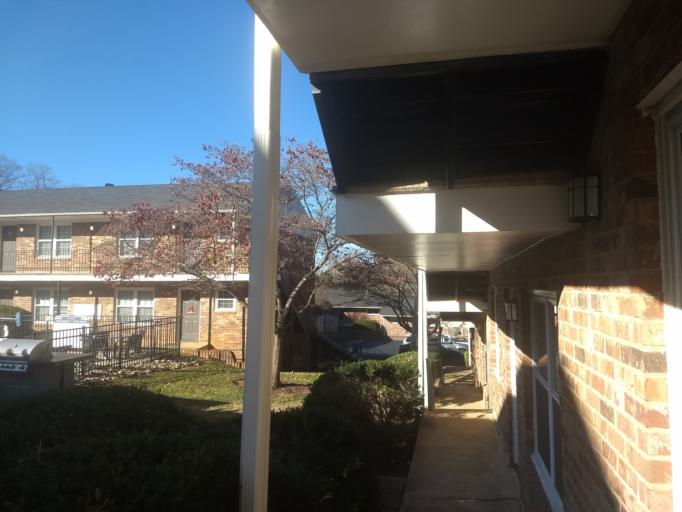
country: US
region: South Carolina
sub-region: Greenville County
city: Wade Hampton
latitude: 34.8705
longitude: -82.3511
